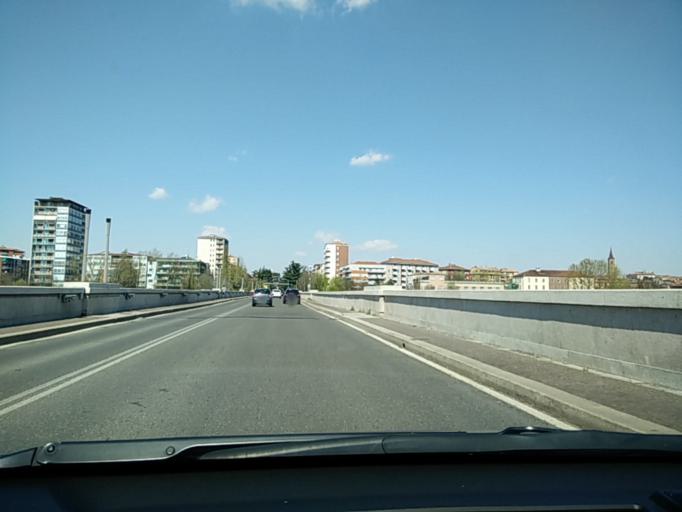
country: IT
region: Lombardy
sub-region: Provincia di Pavia
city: Rotta
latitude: 45.1798
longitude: 9.1465
